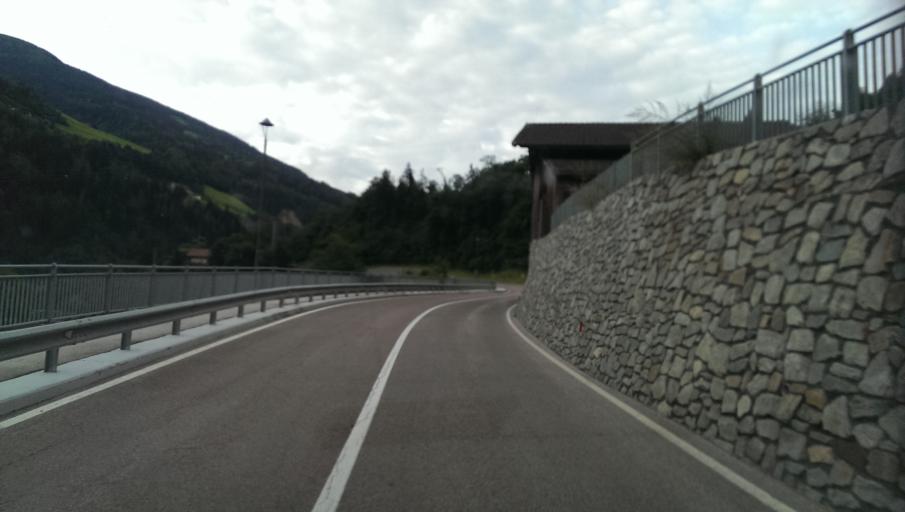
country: IT
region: Trentino-Alto Adige
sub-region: Bolzano
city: Rifiano
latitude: 46.7332
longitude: 11.1994
